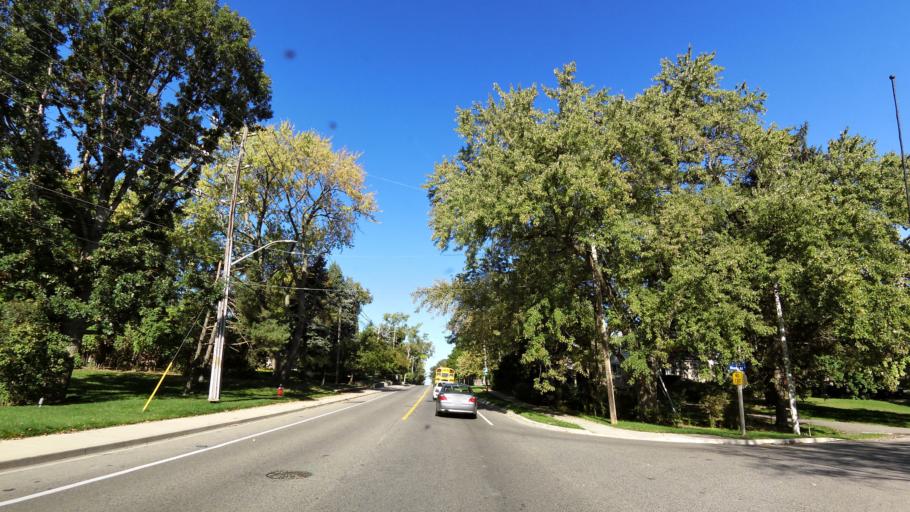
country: CA
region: Ontario
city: Mississauga
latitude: 43.5426
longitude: -79.6114
